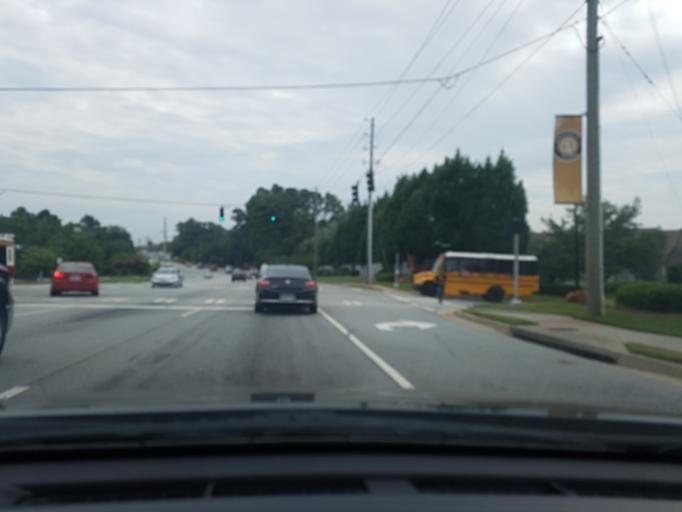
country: US
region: Georgia
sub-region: Gwinnett County
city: Duluth
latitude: 33.9591
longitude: -84.1417
